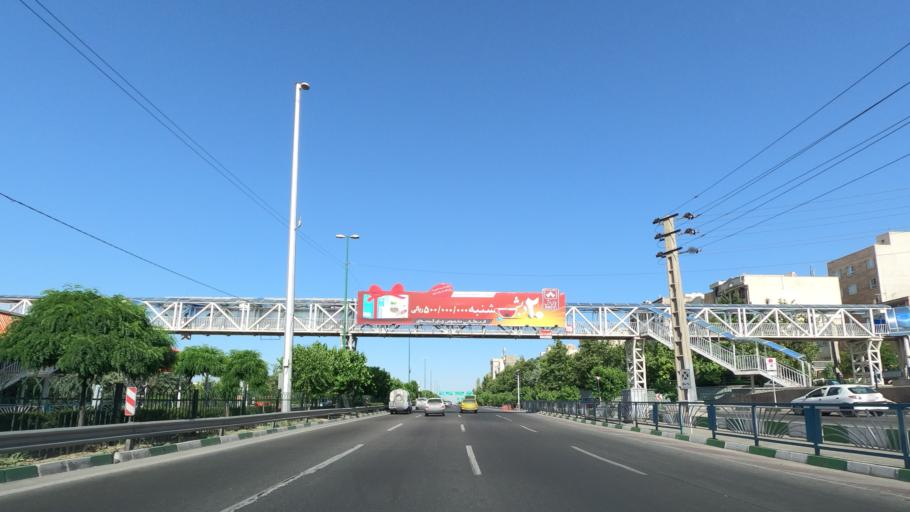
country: IR
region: Tehran
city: Tehran
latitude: 35.7533
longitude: 51.3040
